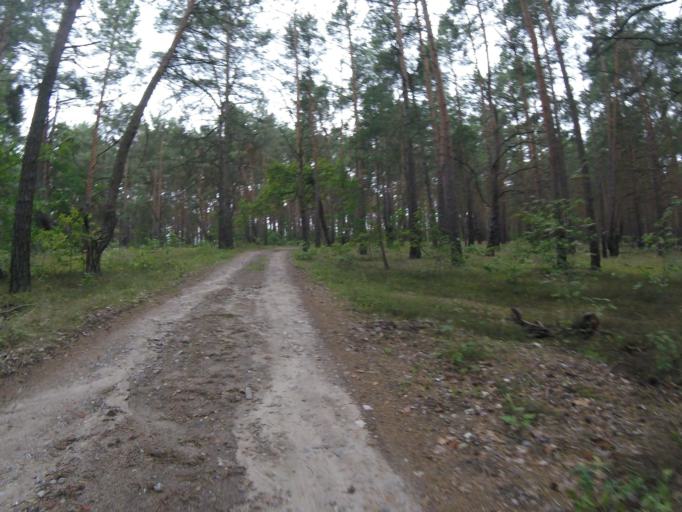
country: DE
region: Brandenburg
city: Bestensee
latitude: 52.2241
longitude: 13.6740
